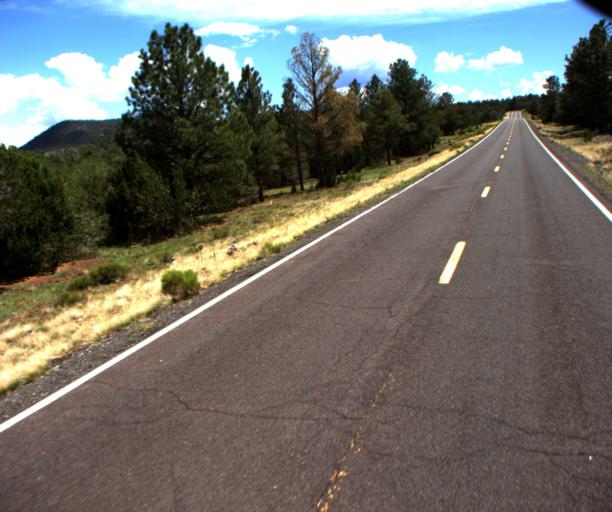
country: US
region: Arizona
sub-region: Coconino County
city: Parks
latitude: 35.5231
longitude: -111.8397
